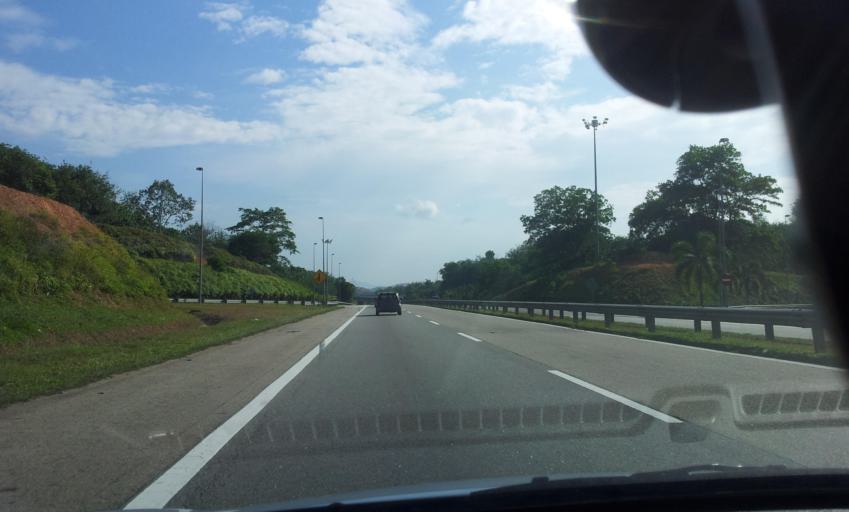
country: MY
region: Pahang
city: Mentekab
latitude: 3.5273
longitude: 102.1748
